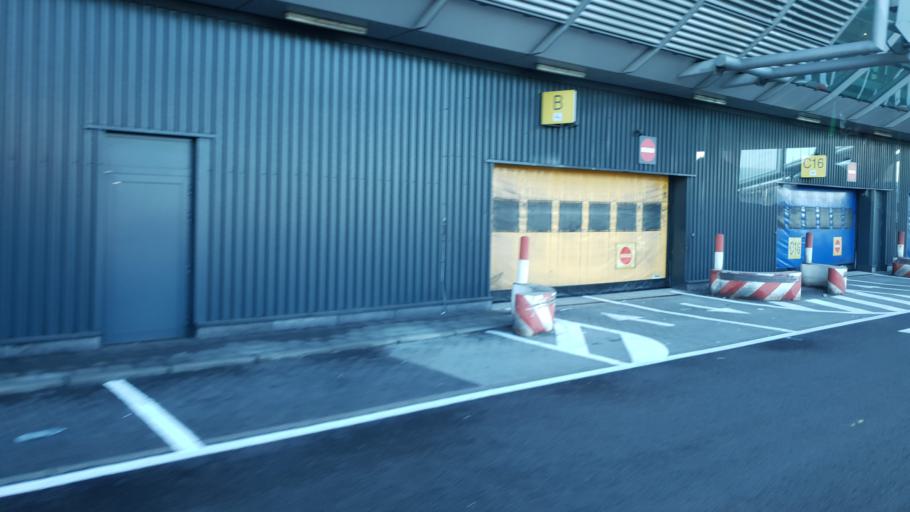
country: BE
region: Flanders
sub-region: Provincie Vlaams-Brabant
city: Zaventem
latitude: 50.9032
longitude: 4.4848
